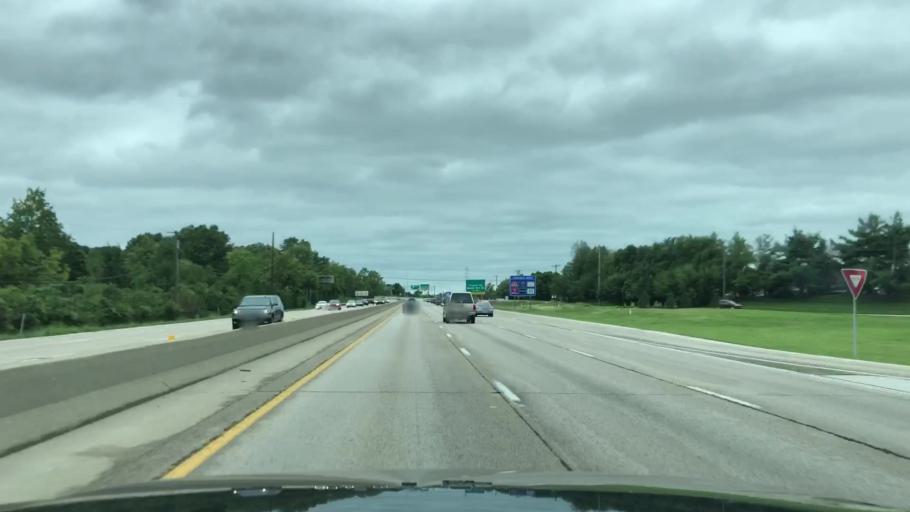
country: US
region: Missouri
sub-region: Saint Louis County
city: Manchester
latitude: 38.6343
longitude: -90.5133
